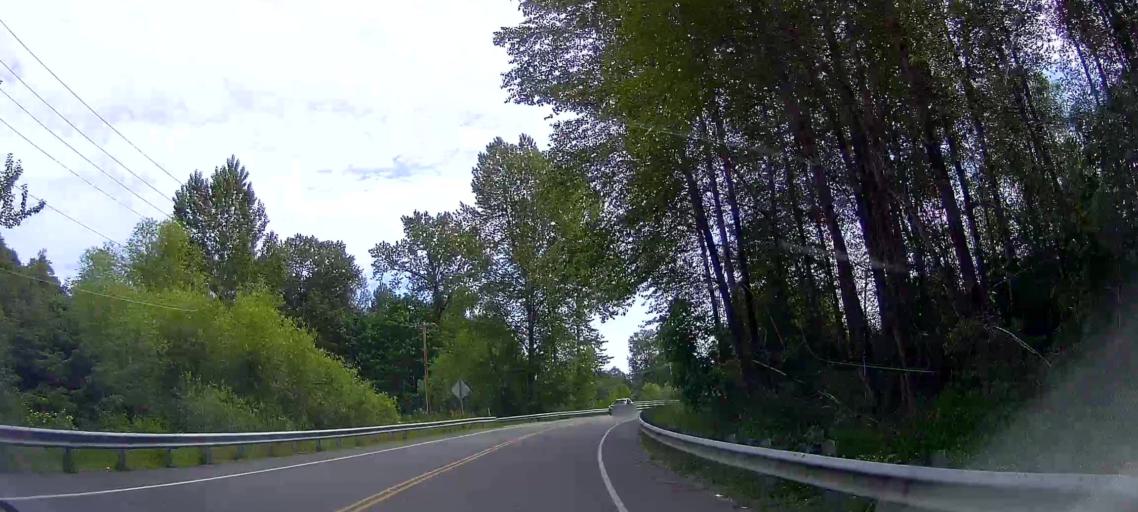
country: US
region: Washington
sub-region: Snohomish County
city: Bryant
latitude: 48.2392
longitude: -122.2066
